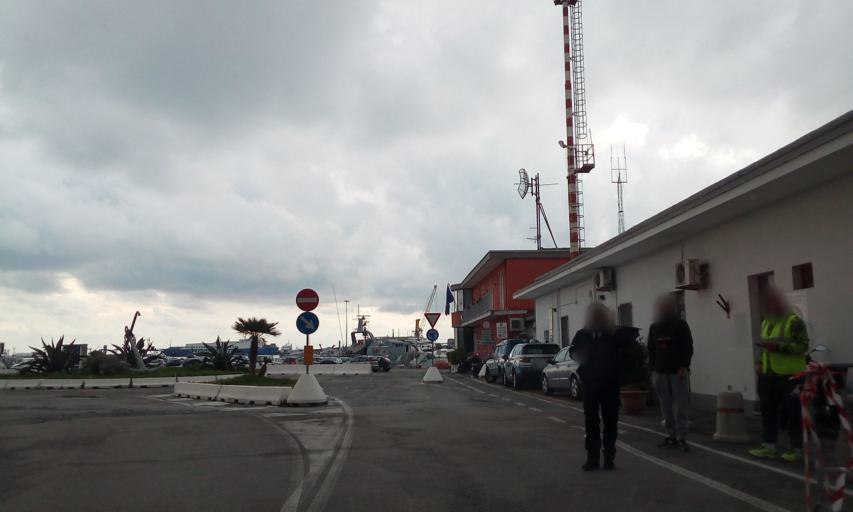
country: IT
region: Campania
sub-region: Provincia di Salerno
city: Vietri sul Mare
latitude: 40.6770
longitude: 14.7514
